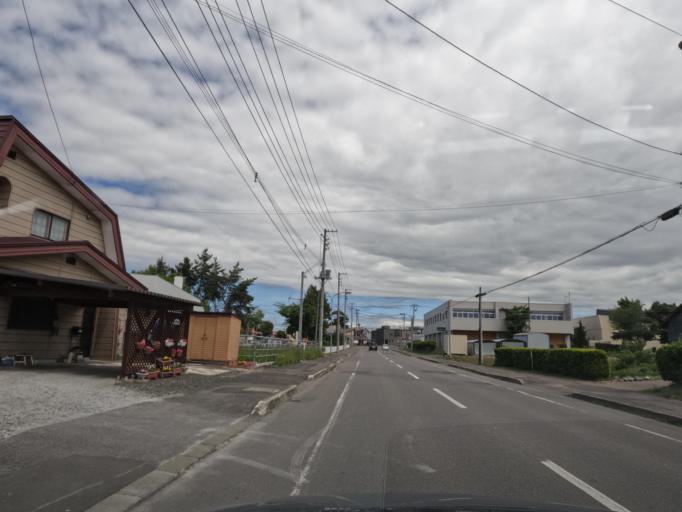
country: JP
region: Hokkaido
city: Shimo-furano
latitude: 43.4581
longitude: 142.4651
